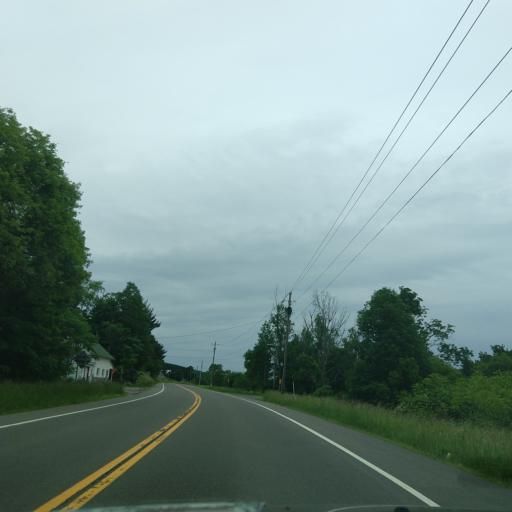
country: US
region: New York
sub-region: Cortland County
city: McGraw
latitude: 42.4836
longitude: -76.0668
